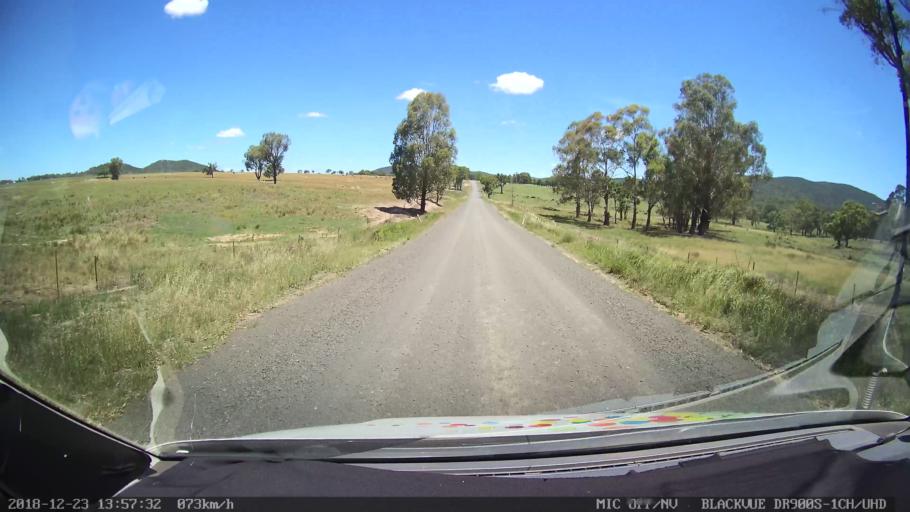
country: AU
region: New South Wales
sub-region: Tamworth Municipality
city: Manilla
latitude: -30.5889
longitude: 151.0937
